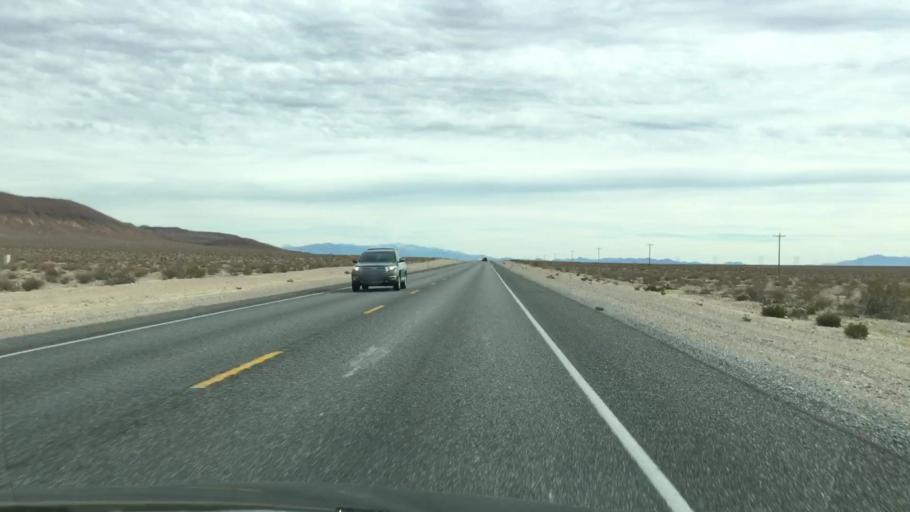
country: US
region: Nevada
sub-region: Nye County
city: Beatty
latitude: 36.7044
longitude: -116.5887
